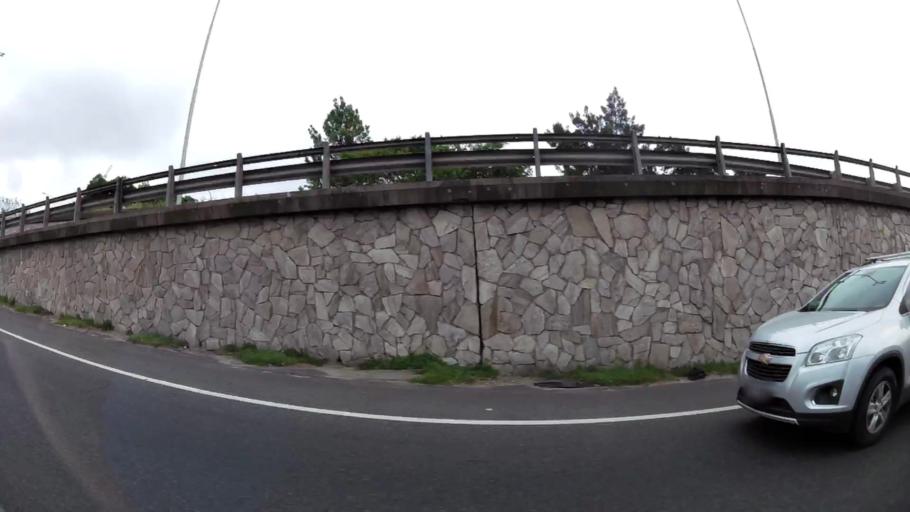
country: AR
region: Buenos Aires
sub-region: Partido de Vicente Lopez
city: Olivos
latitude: -34.5458
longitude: -58.4914
